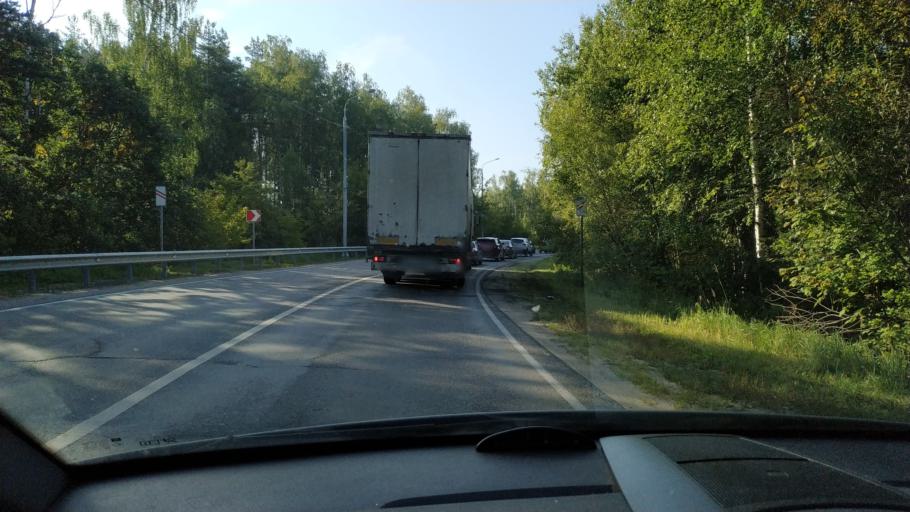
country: RU
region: Moskovskaya
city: Tugolesskiy Bor
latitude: 55.5611
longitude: 39.7017
